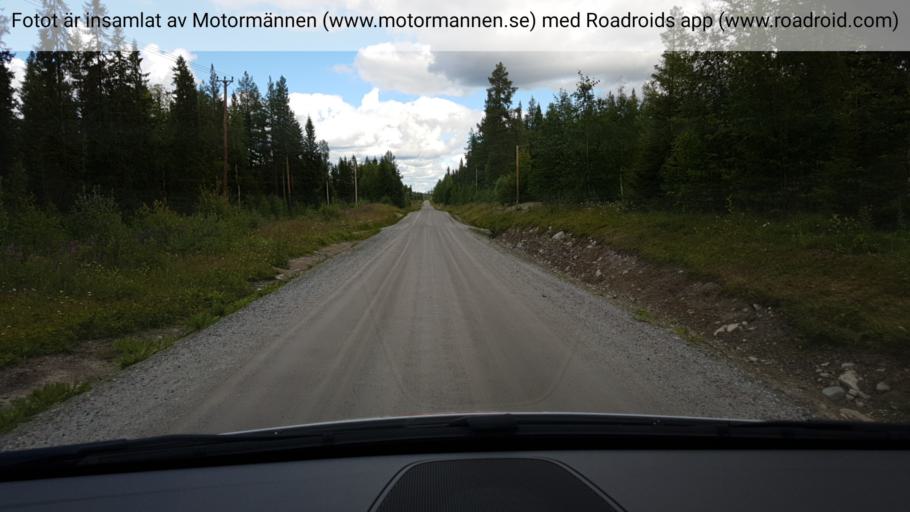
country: SE
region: Jaemtland
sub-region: Braecke Kommun
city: Braecke
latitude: 63.0436
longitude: 15.7253
